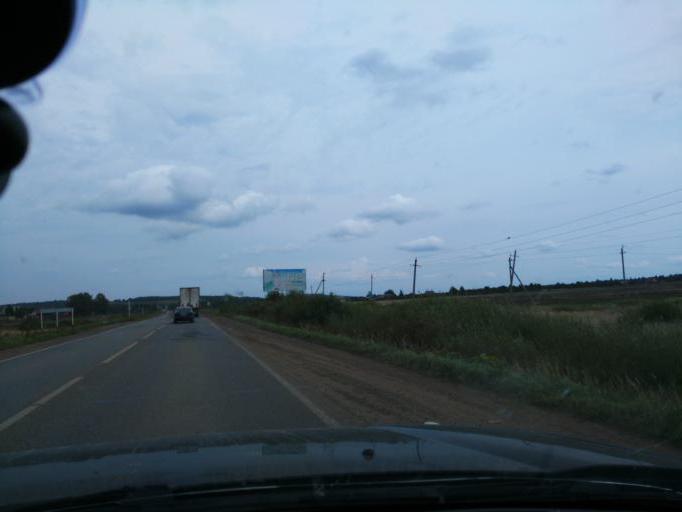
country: RU
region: Perm
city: Kuyeda
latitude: 56.4499
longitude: 55.6050
